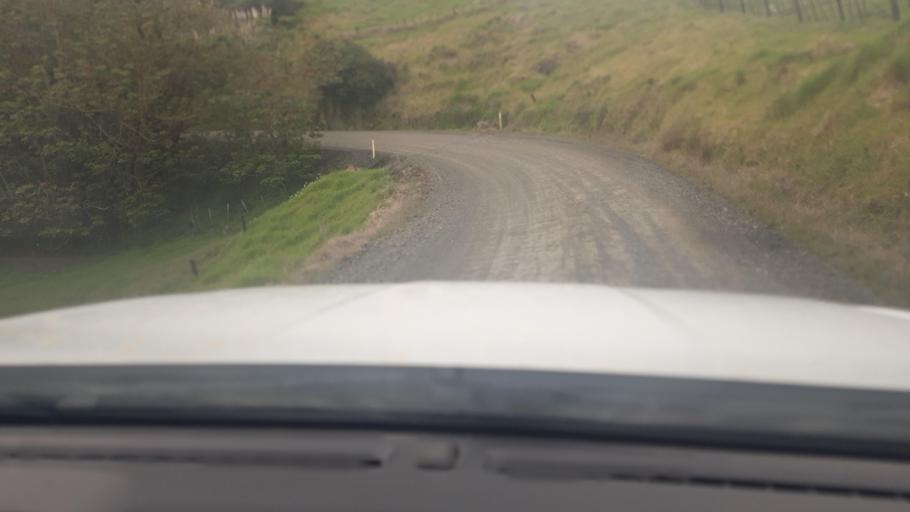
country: NZ
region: Northland
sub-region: Far North District
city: Kaitaia
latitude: -35.0884
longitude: 173.3196
